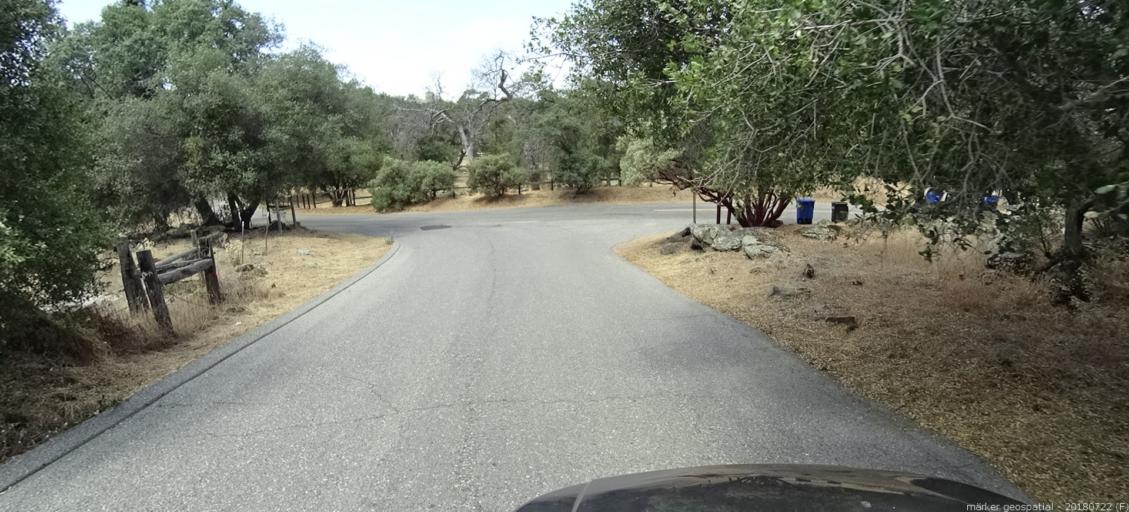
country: US
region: California
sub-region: Madera County
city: Coarsegold
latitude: 37.2833
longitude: -119.7402
